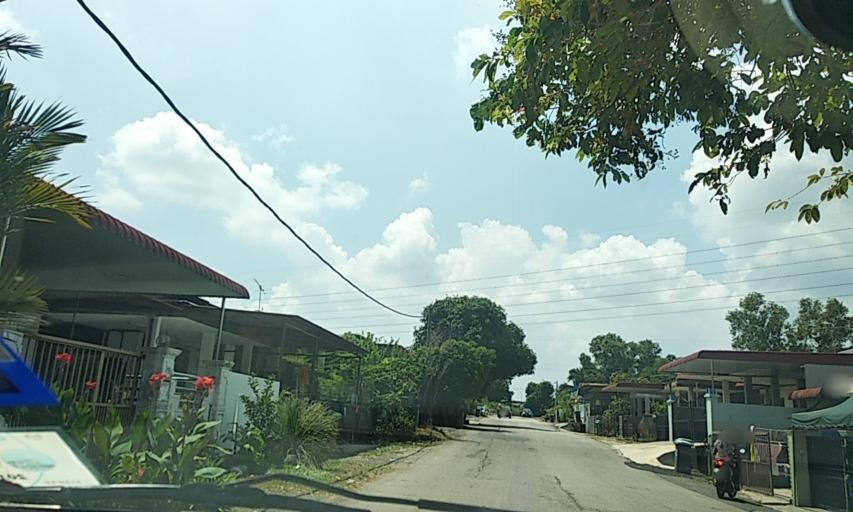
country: MY
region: Kedah
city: Sungai Petani
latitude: 5.6250
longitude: 100.4708
